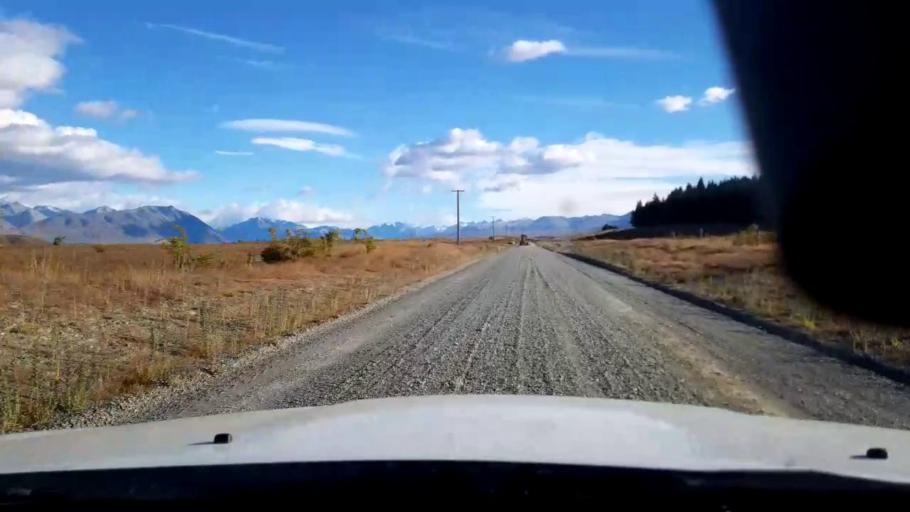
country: NZ
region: Canterbury
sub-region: Timaru District
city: Pleasant Point
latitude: -43.9844
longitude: 170.5067
